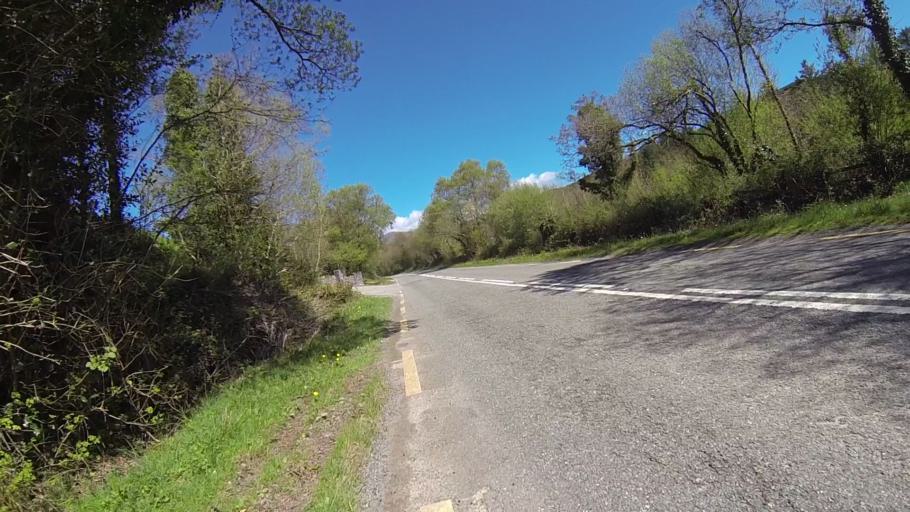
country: IE
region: Munster
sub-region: Ciarrai
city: Kenmare
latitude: 51.8987
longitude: -9.5996
